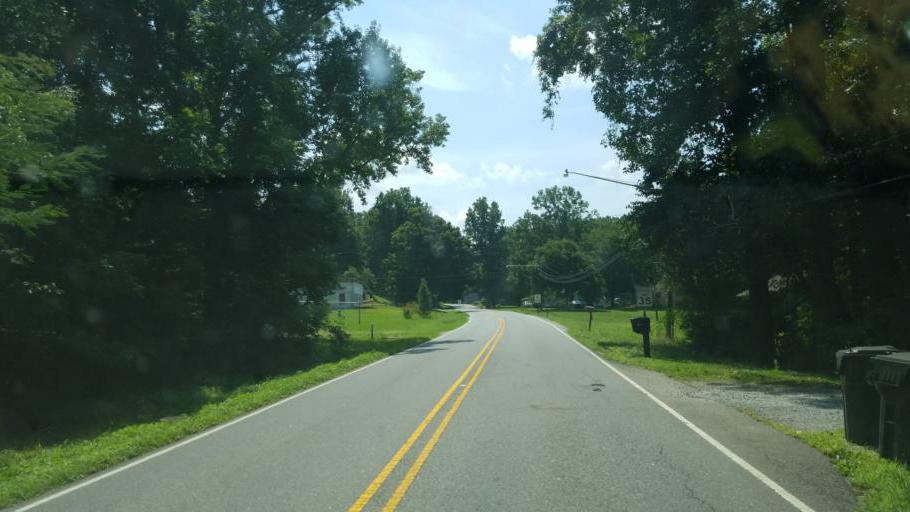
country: US
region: North Carolina
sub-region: Gaston County
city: Cherryville
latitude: 35.3900
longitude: -81.3896
